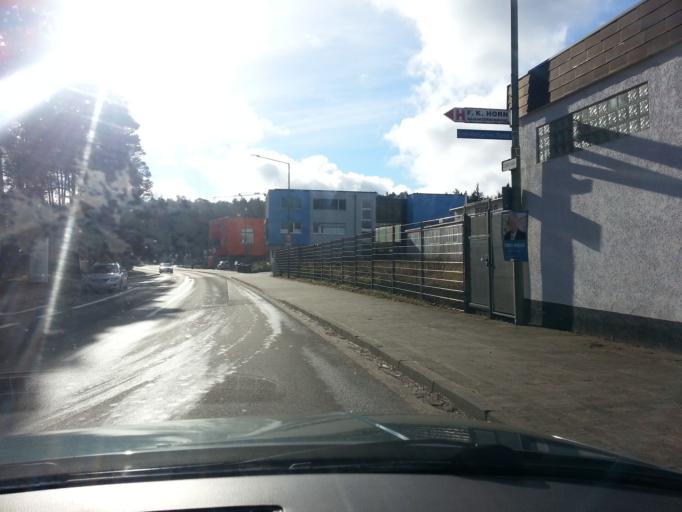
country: DE
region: Rheinland-Pfalz
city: Katzweiler
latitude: 49.4632
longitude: 7.6929
